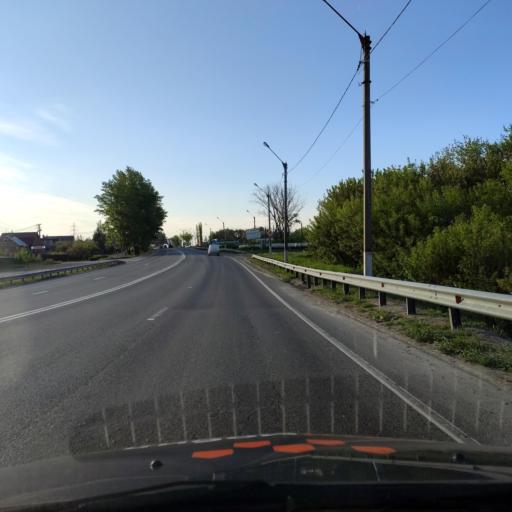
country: RU
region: Lipetsk
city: Yelets
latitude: 52.5965
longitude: 38.4781
